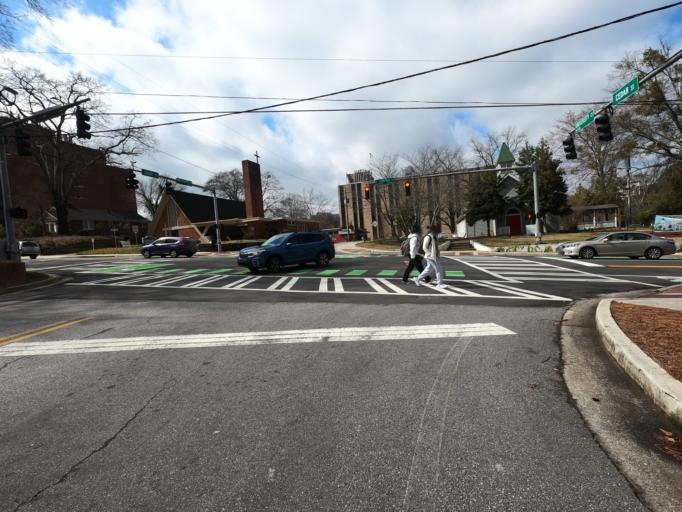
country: US
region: Georgia
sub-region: Clarke County
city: Athens
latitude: 33.9476
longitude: -83.3778
